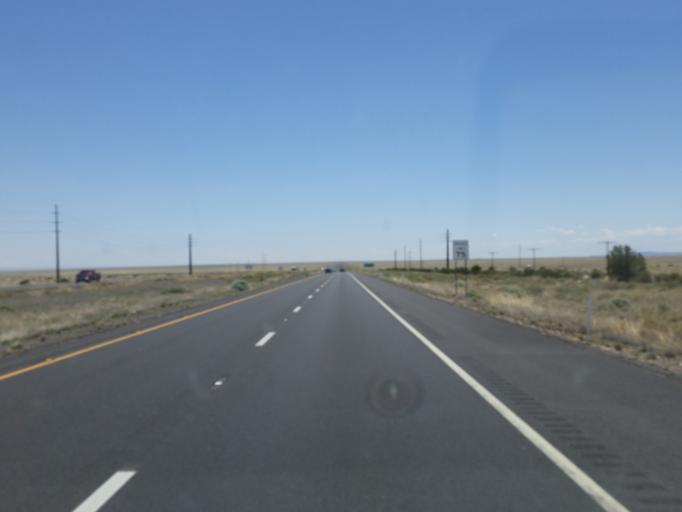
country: US
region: Arizona
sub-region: Coconino County
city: Flagstaff
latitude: 35.1573
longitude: -111.2611
